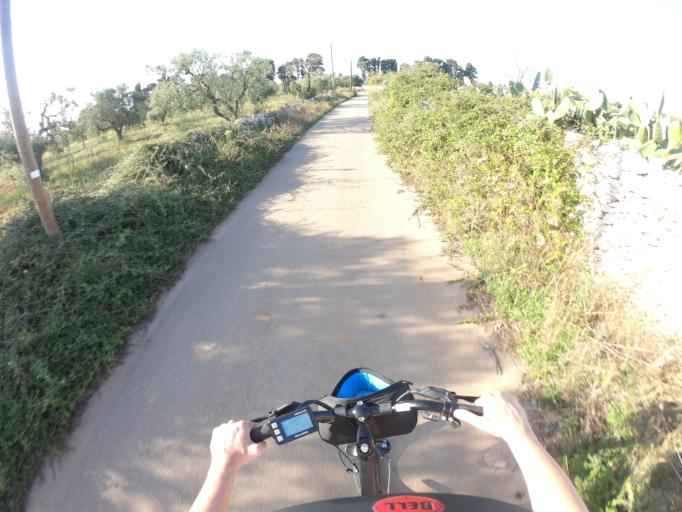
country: IT
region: Apulia
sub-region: Provincia di Lecce
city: Castrignano del Capo
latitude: 39.8378
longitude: 18.3549
